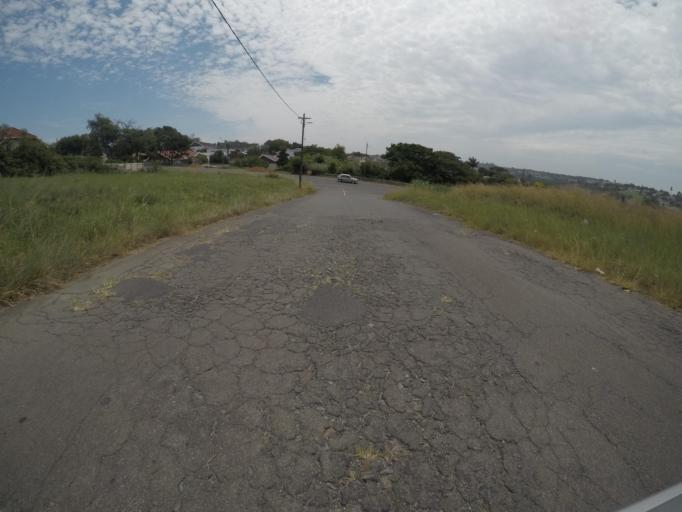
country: ZA
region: Eastern Cape
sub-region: Buffalo City Metropolitan Municipality
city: East London
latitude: -32.9836
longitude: 27.8687
